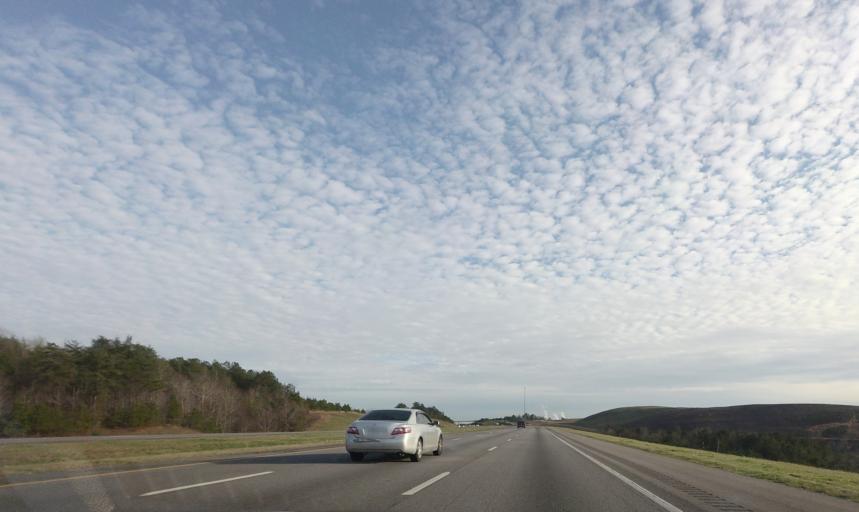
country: US
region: Alabama
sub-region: Walker County
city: Dora
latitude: 33.6987
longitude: -87.1322
